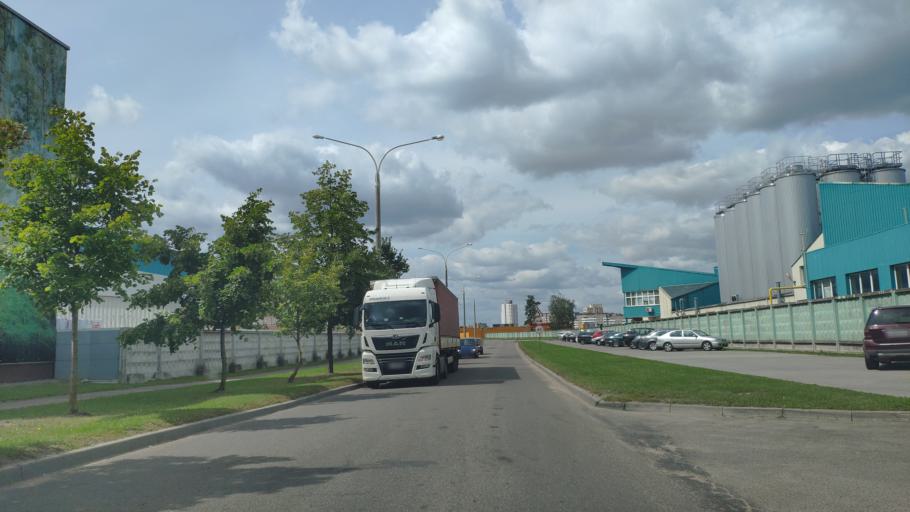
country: BY
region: Minsk
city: Vyaliki Trastsyanets
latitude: 53.8651
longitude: 27.6976
